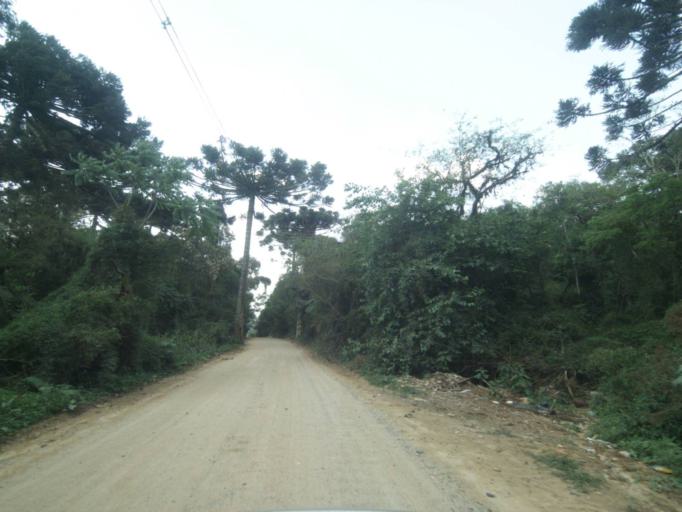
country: BR
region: Parana
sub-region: Sao Jose Dos Pinhais
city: Sao Jose dos Pinhais
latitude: -25.5428
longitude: -49.2349
